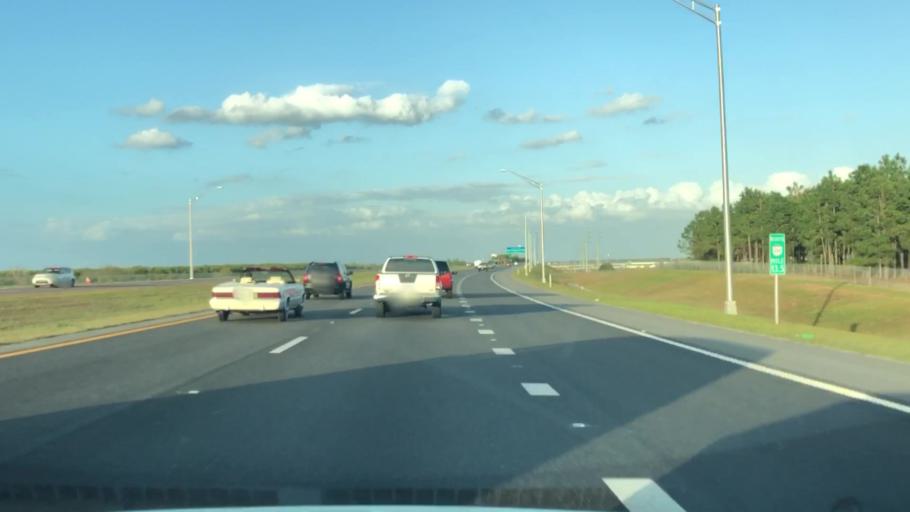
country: US
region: Florida
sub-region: Orange County
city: Oakland
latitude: 28.4550
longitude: -81.6398
